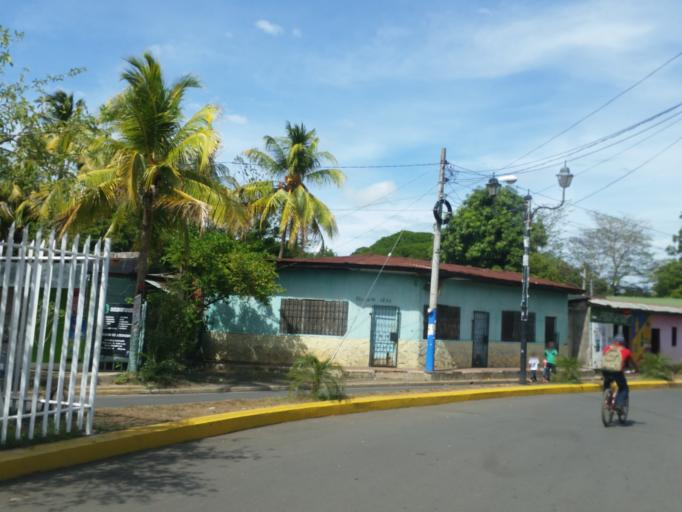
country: NI
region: Masaya
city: Nindiri
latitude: 12.0025
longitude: -86.1198
